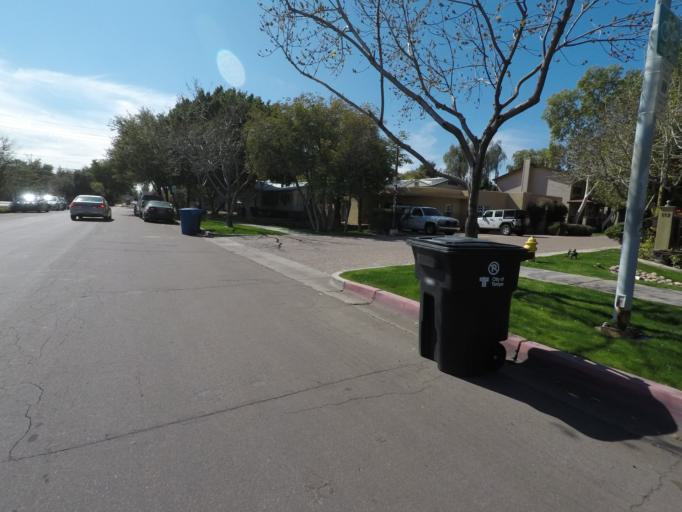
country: US
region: Arizona
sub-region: Maricopa County
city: Tempe Junction
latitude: 33.4197
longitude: -111.9424
